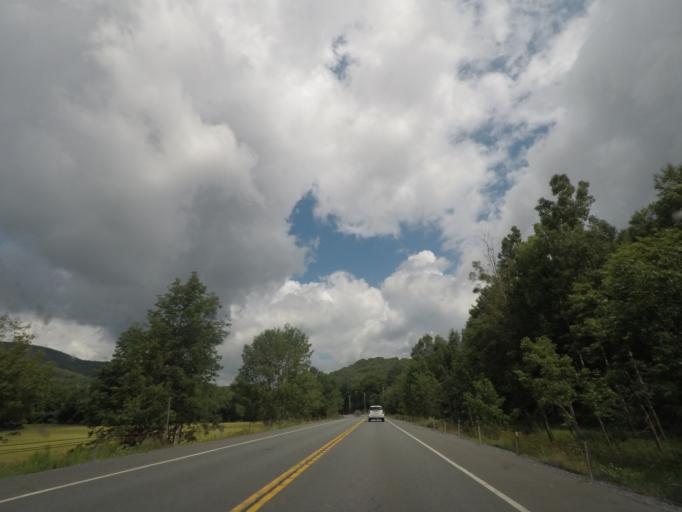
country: US
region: Massachusetts
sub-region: Berkshire County
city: Williamstown
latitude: 42.6555
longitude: -73.3656
